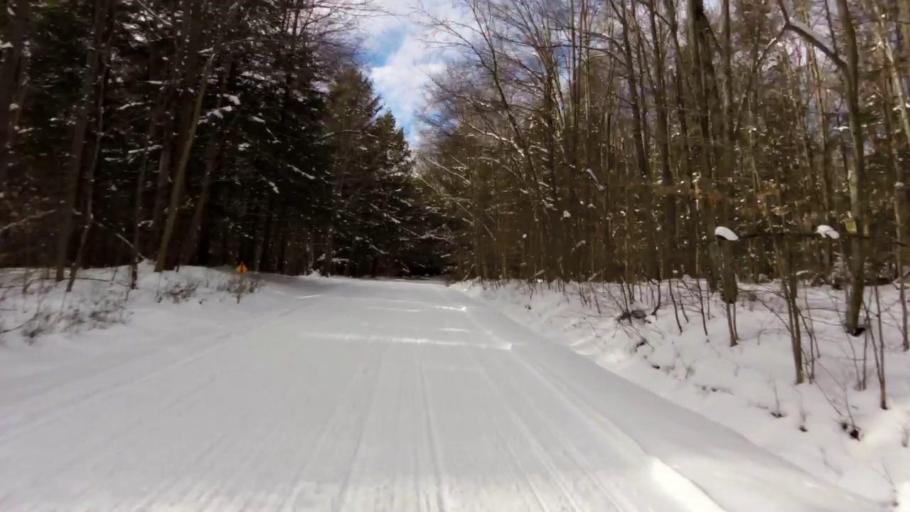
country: US
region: Pennsylvania
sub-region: McKean County
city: Bradford
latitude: 42.0250
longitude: -78.6960
